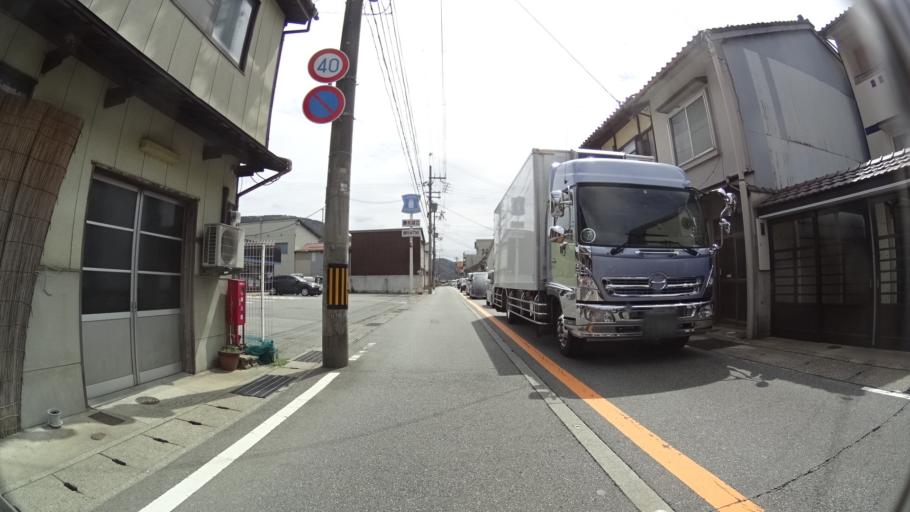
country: JP
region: Hyogo
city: Toyooka
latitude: 35.6138
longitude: 134.8056
